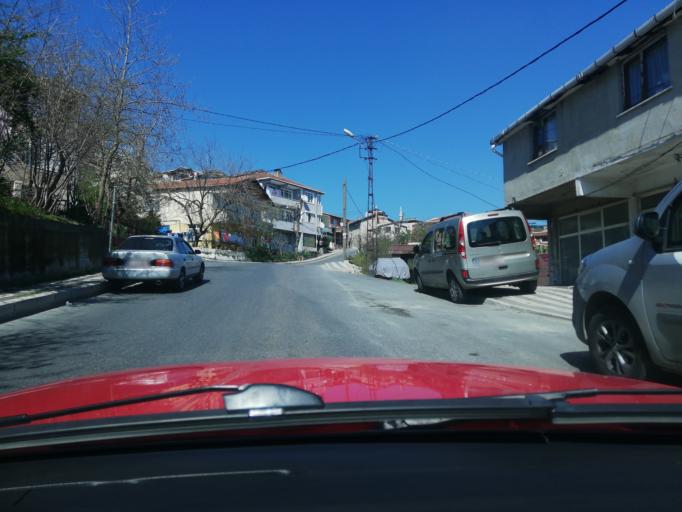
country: TR
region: Istanbul
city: Mahmut Sevket Pasa
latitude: 41.1147
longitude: 29.1145
